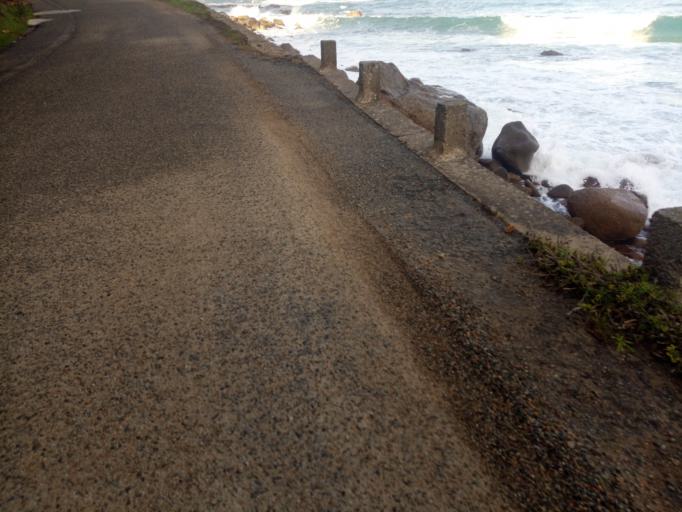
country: FR
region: Corsica
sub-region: Departement de la Corse-du-Sud
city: Appietto
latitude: 42.0409
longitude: 8.7412
